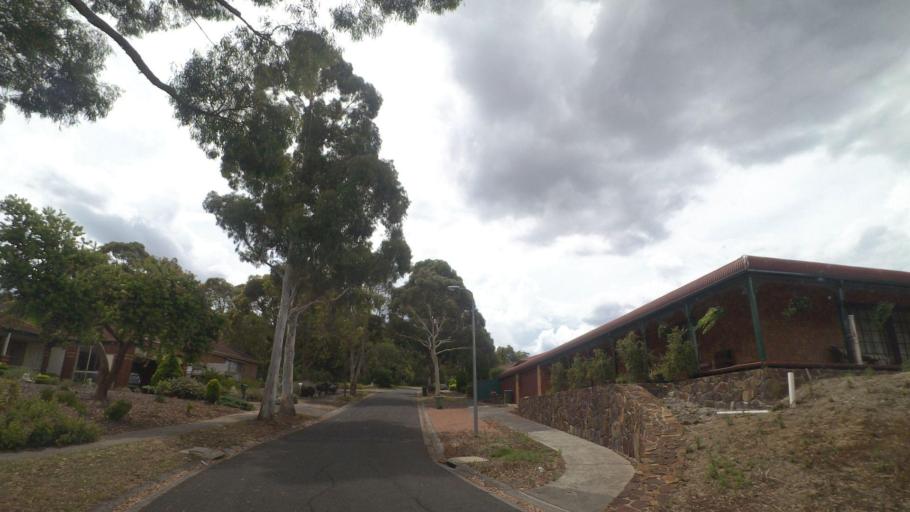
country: AU
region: Victoria
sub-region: Maroondah
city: Croydon South
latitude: -37.8196
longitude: 145.2809
